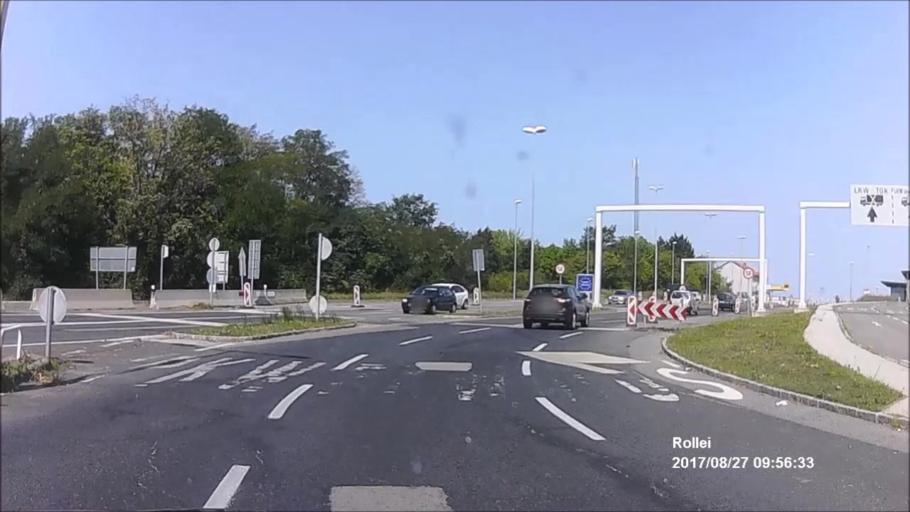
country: AT
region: Burgenland
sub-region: Eisenstadt-Umgebung
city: Klingenbach
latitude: 47.7410
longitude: 16.5456
